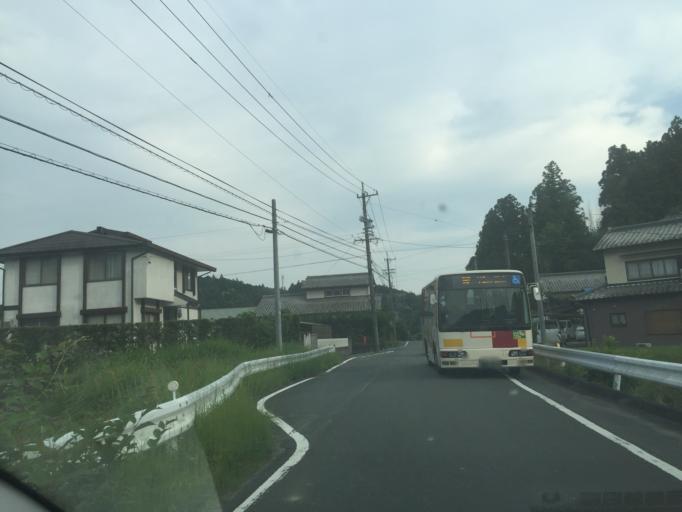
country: JP
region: Shizuoka
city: Kakegawa
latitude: 34.8199
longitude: 138.0179
